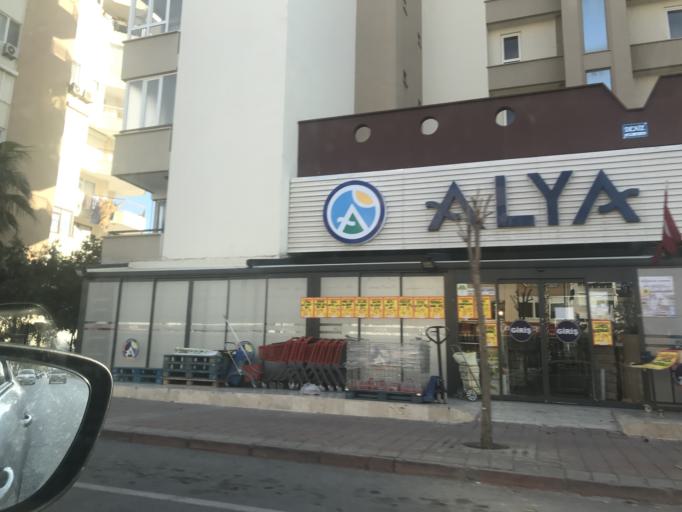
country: TR
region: Antalya
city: Antalya
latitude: 36.8542
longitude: 30.7773
